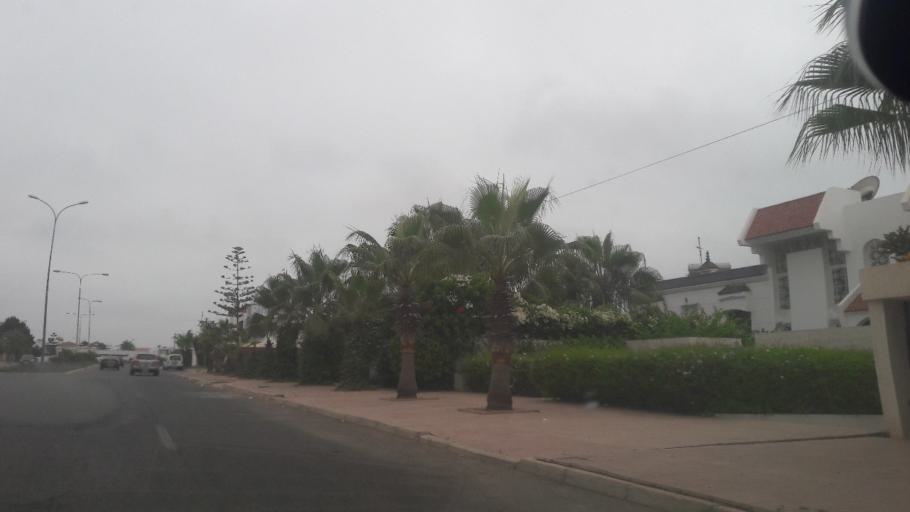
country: MA
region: Souss-Massa-Draa
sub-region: Agadir-Ida-ou-Tnan
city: Agadir
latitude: 30.3912
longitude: -9.5941
